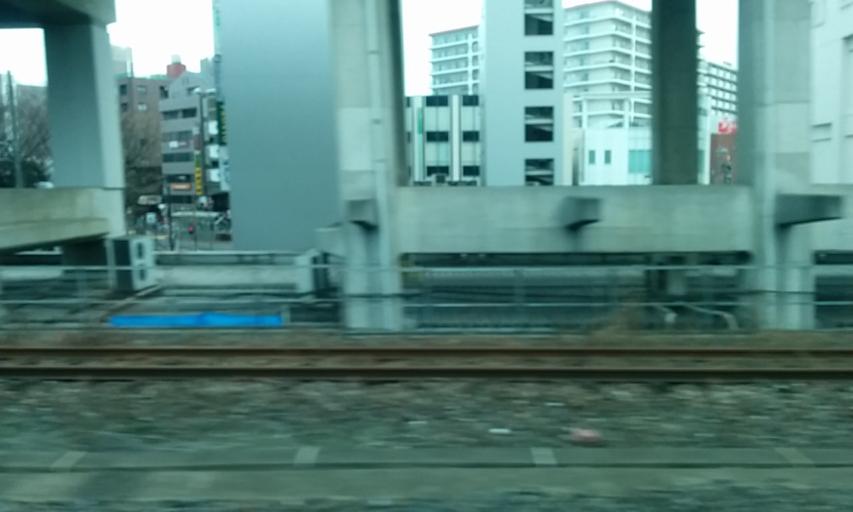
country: JP
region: Saitama
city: Kawaguchi
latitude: 35.7544
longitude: 139.7367
